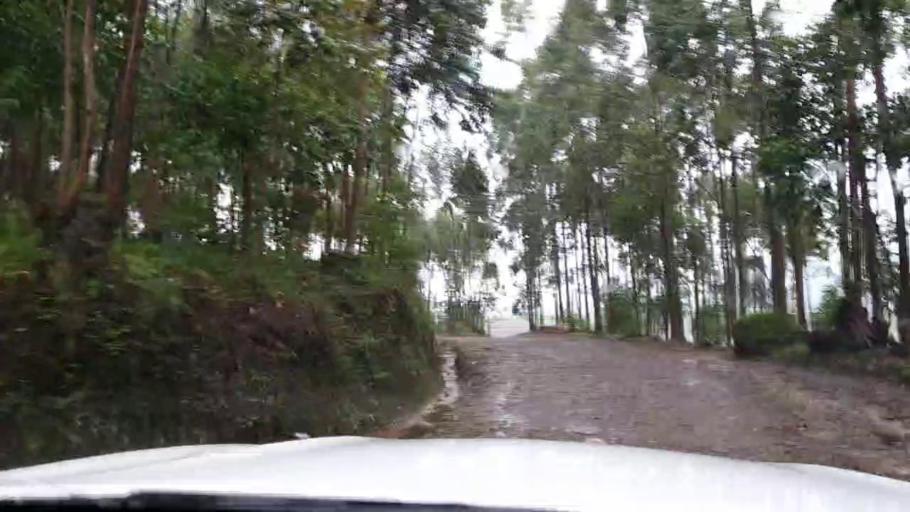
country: RW
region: Western Province
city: Cyangugu
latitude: -2.4733
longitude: 29.0331
